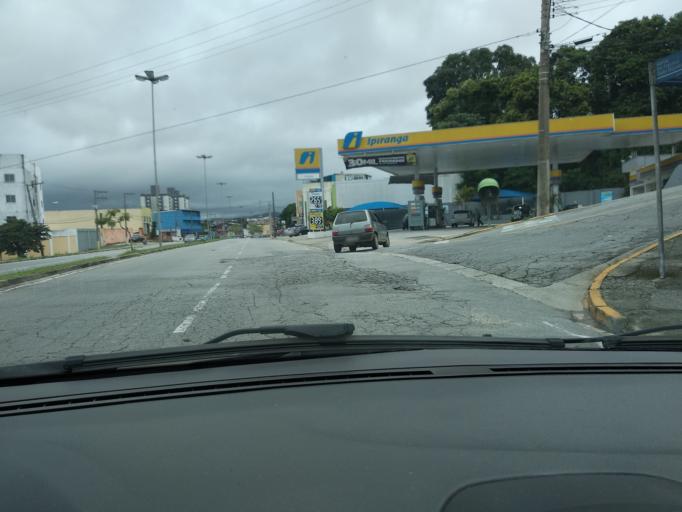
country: BR
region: Sao Paulo
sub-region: Mogi das Cruzes
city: Mogi das Cruzes
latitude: -23.5419
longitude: -46.1871
